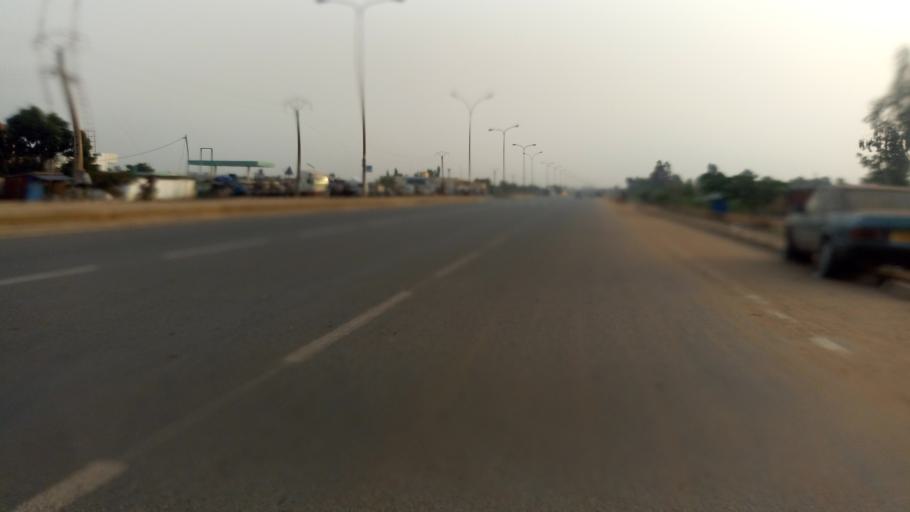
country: TG
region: Maritime
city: Lome
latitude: 6.2698
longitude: 1.2097
